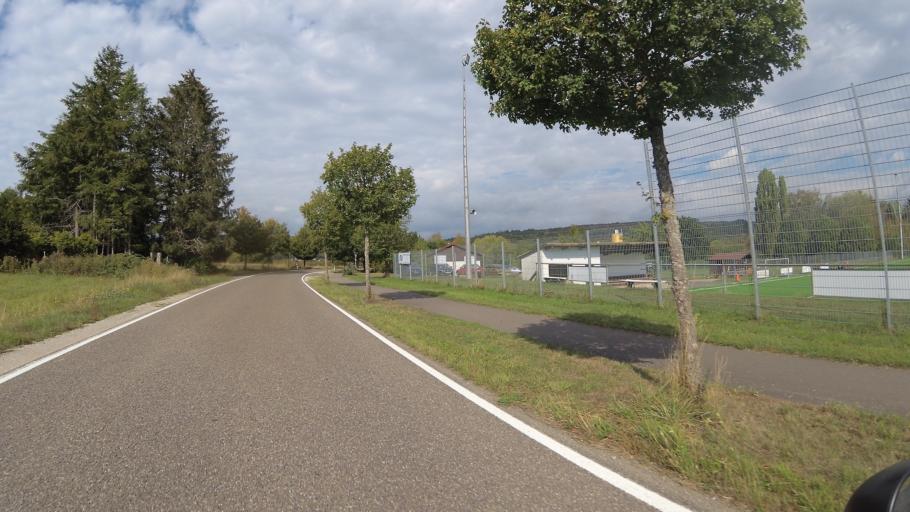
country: DE
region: Saarland
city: Gersheim
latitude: 49.1336
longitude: 7.1975
